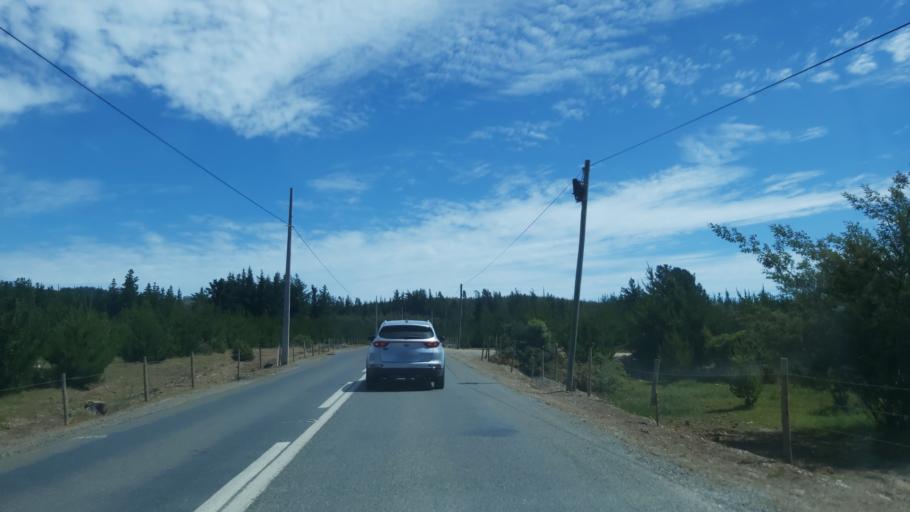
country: CL
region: Maule
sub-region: Provincia de Talca
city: Constitucion
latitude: -35.5358
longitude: -72.5456
